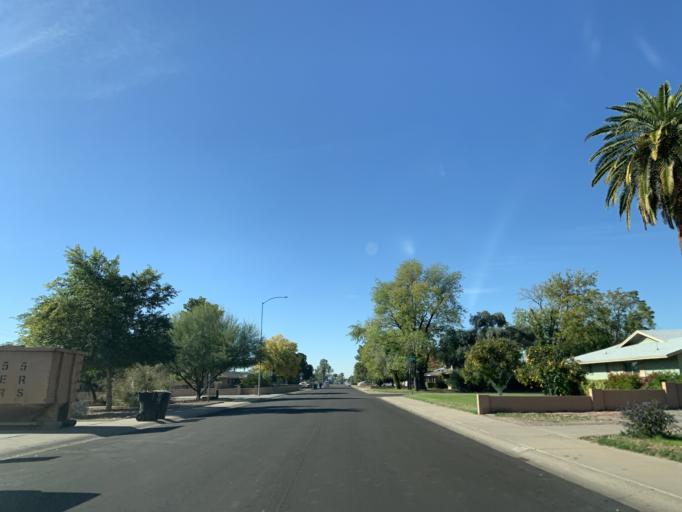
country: US
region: Arizona
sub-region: Maricopa County
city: Mesa
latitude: 33.4162
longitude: -111.8603
